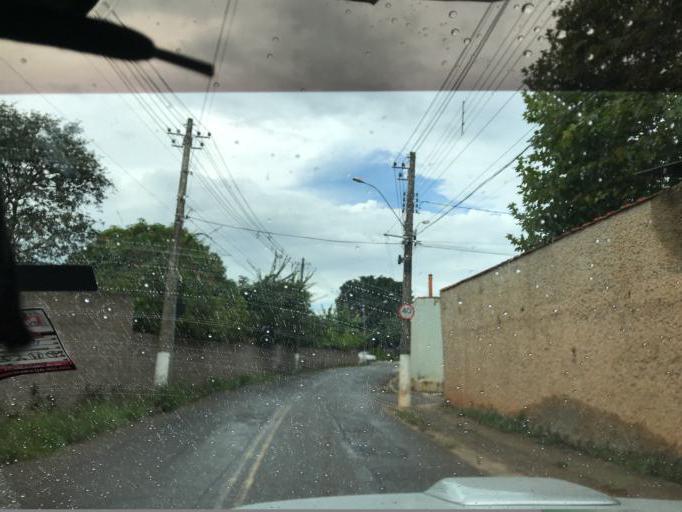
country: BR
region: Minas Gerais
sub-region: Tres Coracoes
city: Tres Coracoes
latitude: -21.7067
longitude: -45.2528
